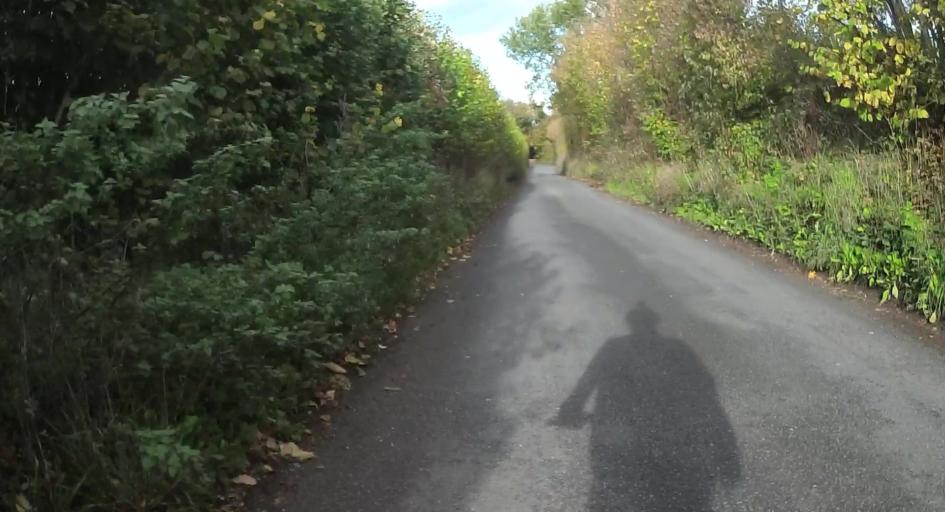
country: GB
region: England
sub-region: Hampshire
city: Basingstoke
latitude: 51.3182
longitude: -1.0719
